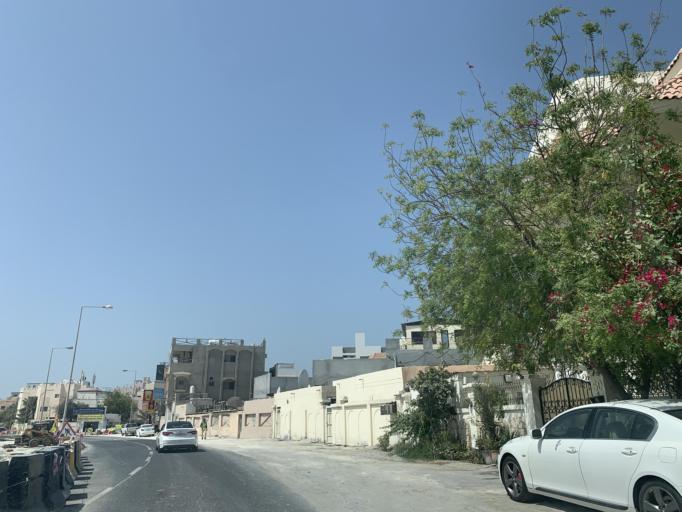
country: BH
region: Muharraq
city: Al Hadd
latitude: 26.2674
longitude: 50.6538
